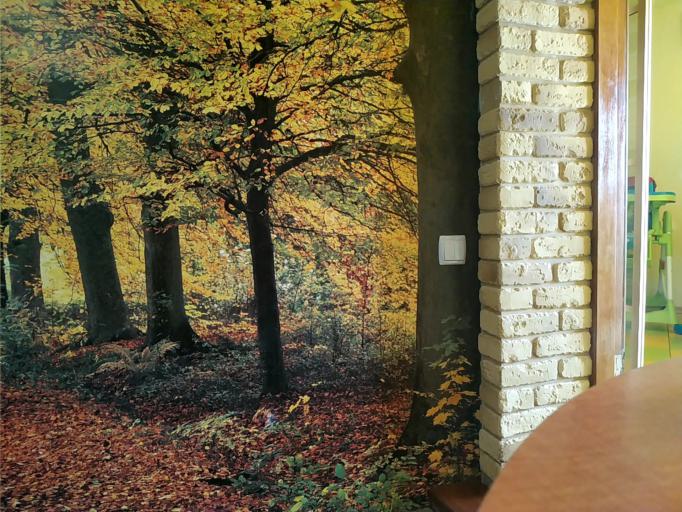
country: RU
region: Vologda
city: Nelazskoye
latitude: 59.4869
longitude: 37.6048
